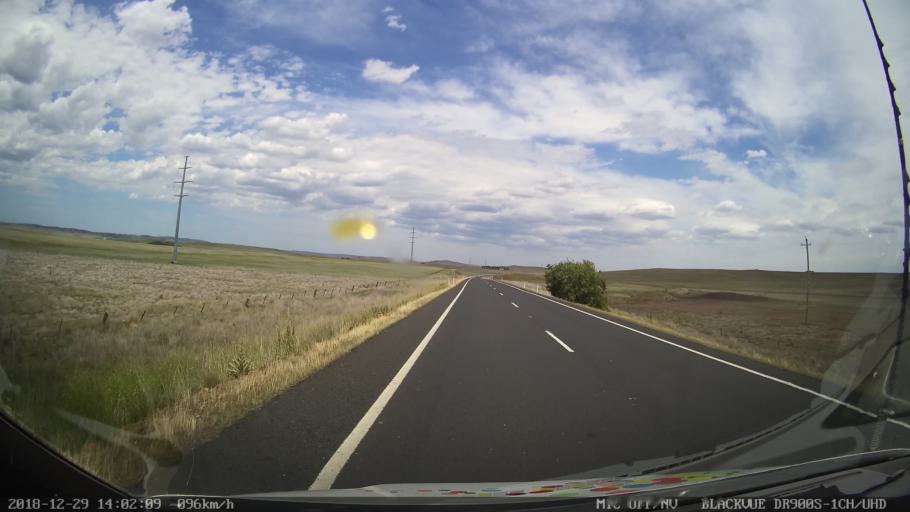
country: AU
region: New South Wales
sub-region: Cooma-Monaro
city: Cooma
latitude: -36.2845
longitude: 149.1742
